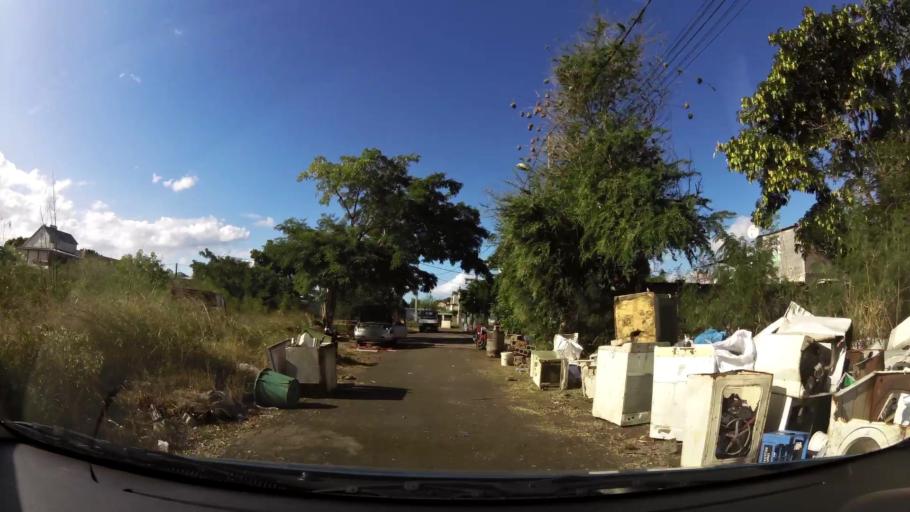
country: MU
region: Black River
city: Albion
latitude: -20.1999
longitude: 57.4119
